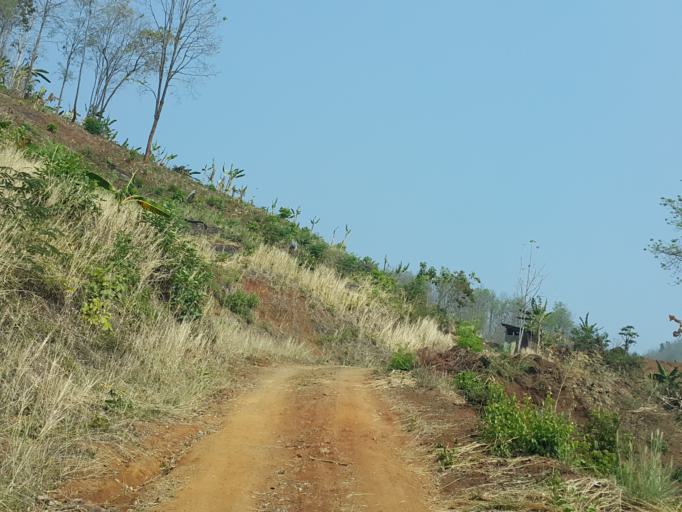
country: TH
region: Chiang Mai
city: Mae On
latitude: 18.7775
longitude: 99.2361
